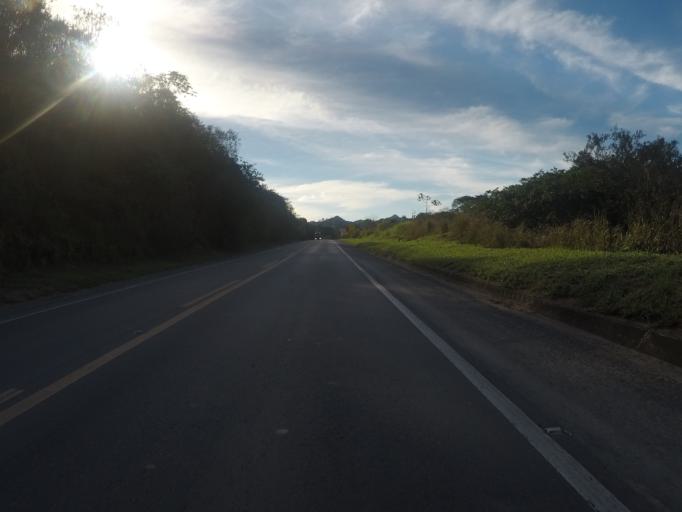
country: BR
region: Espirito Santo
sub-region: Fundao
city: Fundao
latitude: -19.8830
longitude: -40.4161
